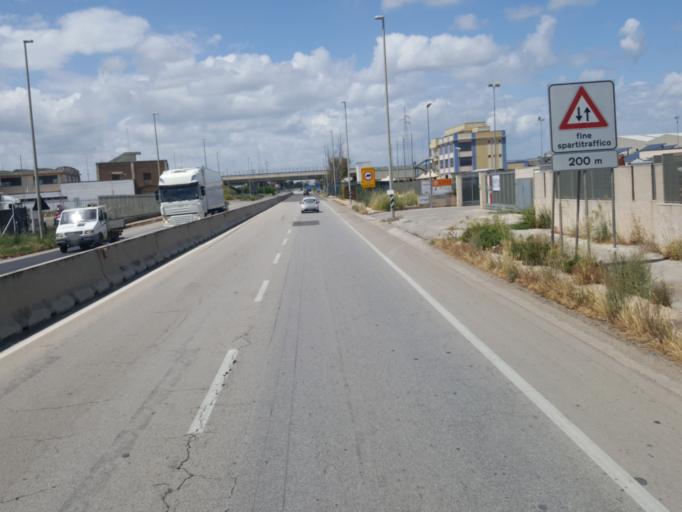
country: IT
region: Apulia
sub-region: Provincia di Bari
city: Modugno
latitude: 41.0908
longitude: 16.7609
